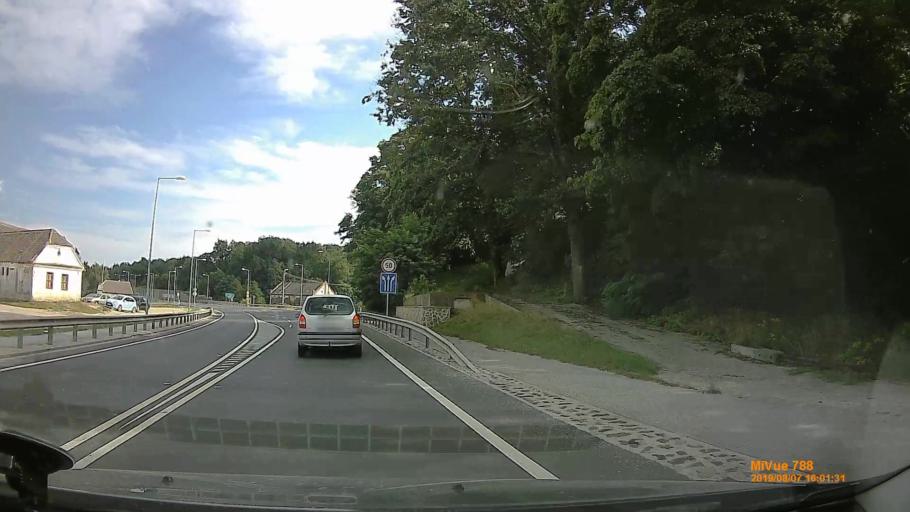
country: HU
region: Vas
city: Kormend
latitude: 46.9883
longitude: 16.6177
